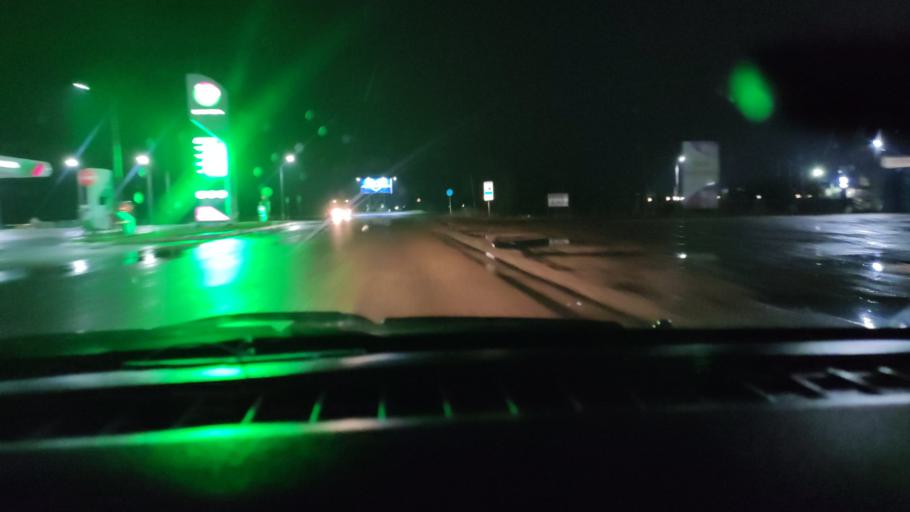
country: RU
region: Udmurtiya
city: Votkinsk
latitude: 57.0429
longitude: 54.0331
